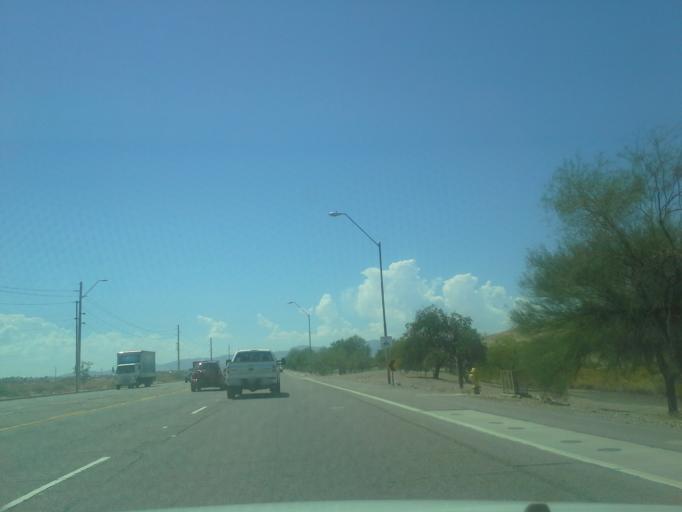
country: US
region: Arizona
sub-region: Maricopa County
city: Youngtown
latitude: 33.5365
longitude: -112.2993
